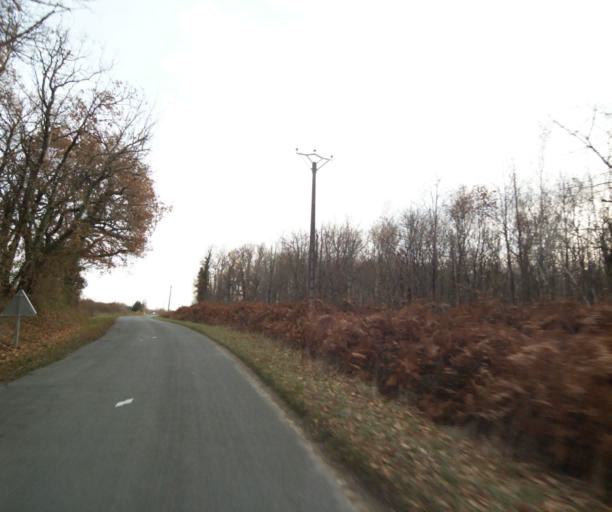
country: FR
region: Poitou-Charentes
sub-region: Departement de la Charente-Maritime
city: Fontcouverte
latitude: 45.8038
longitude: -0.5793
